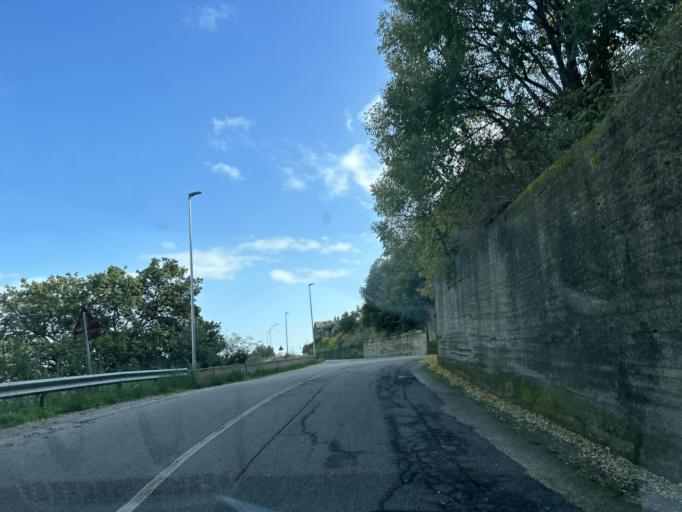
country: IT
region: Calabria
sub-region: Provincia di Catanzaro
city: Montepaone
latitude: 38.7214
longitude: 16.5034
